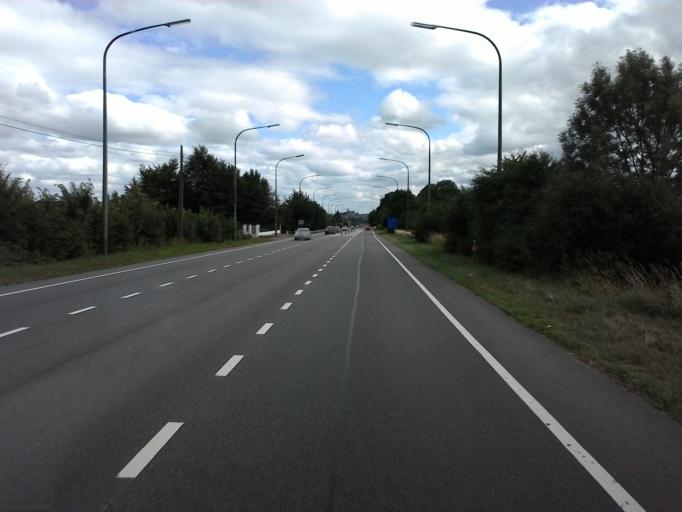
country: BE
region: Wallonia
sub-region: Province du Luxembourg
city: Arlon
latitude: 49.7097
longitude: 5.8029
